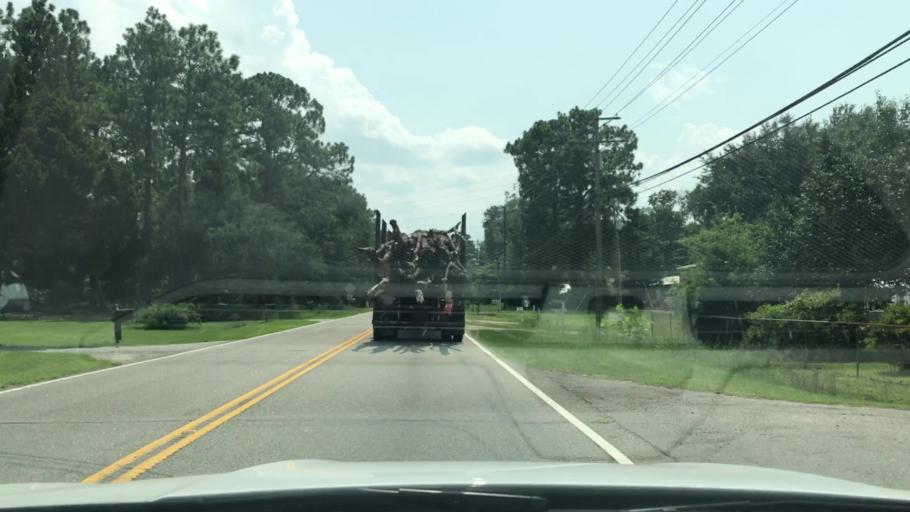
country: US
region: South Carolina
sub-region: Georgetown County
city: Georgetown
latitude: 33.4353
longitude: -79.2768
